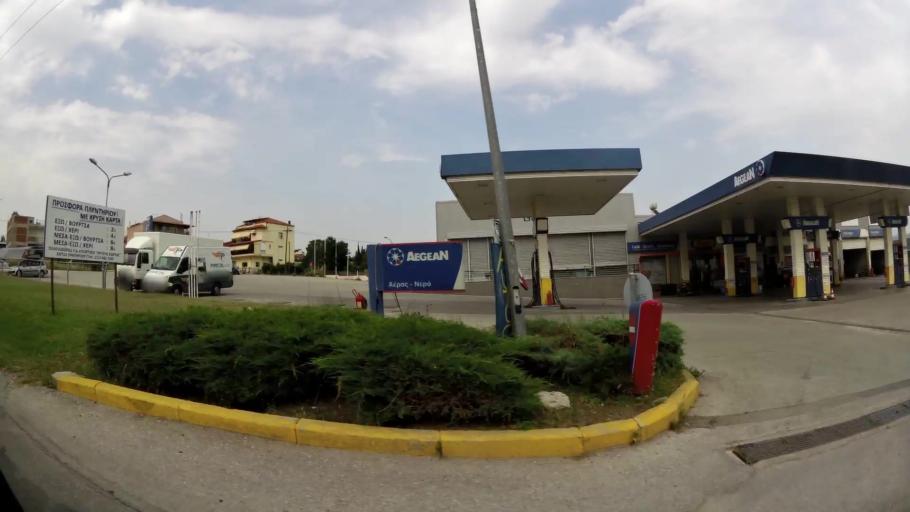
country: GR
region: Central Macedonia
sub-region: Nomos Thessalonikis
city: Efkarpia
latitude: 40.7016
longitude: 22.9301
